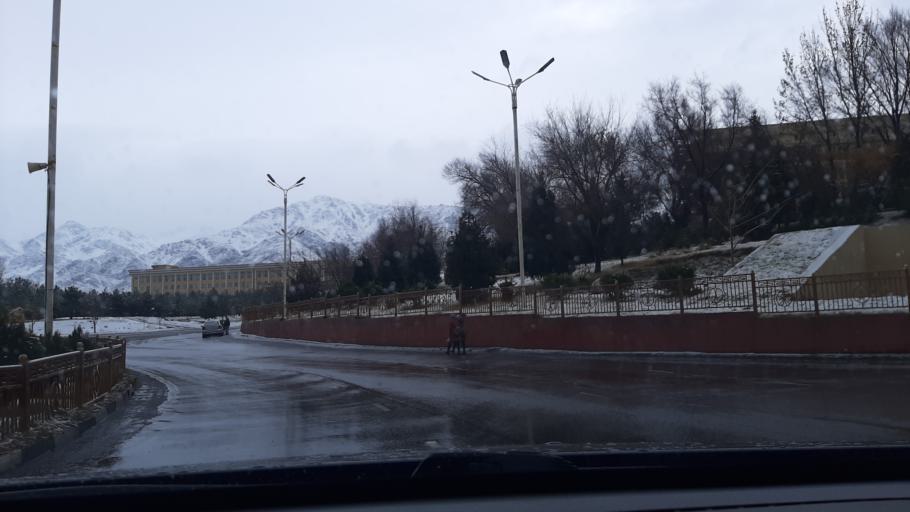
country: TJ
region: Viloyati Sughd
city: Khujand
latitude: 40.3023
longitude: 69.6147
